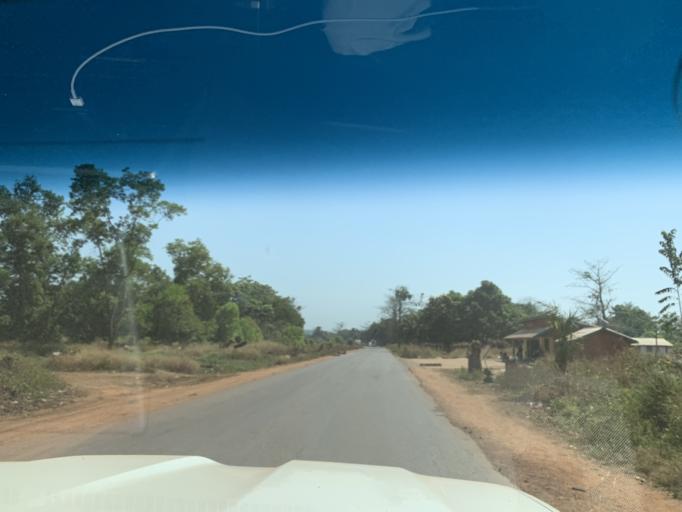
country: GN
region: Kindia
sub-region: Kindia
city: Kindia
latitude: 10.0043
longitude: -12.7729
